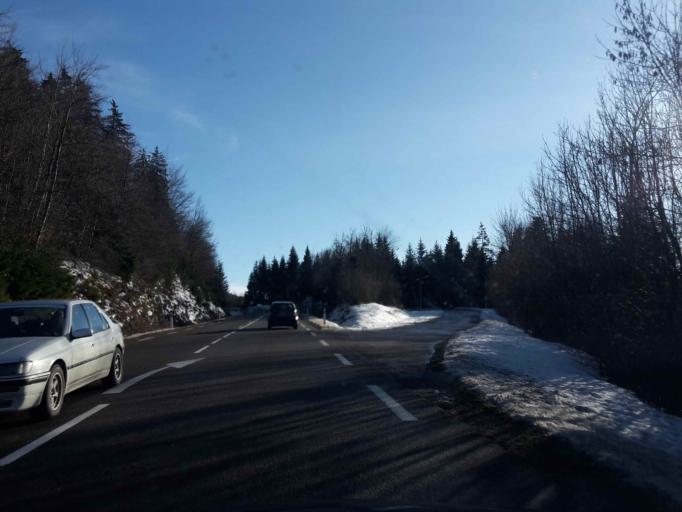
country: FR
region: Franche-Comte
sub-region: Departement du Doubs
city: Doubs
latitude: 47.0032
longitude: 6.3268
